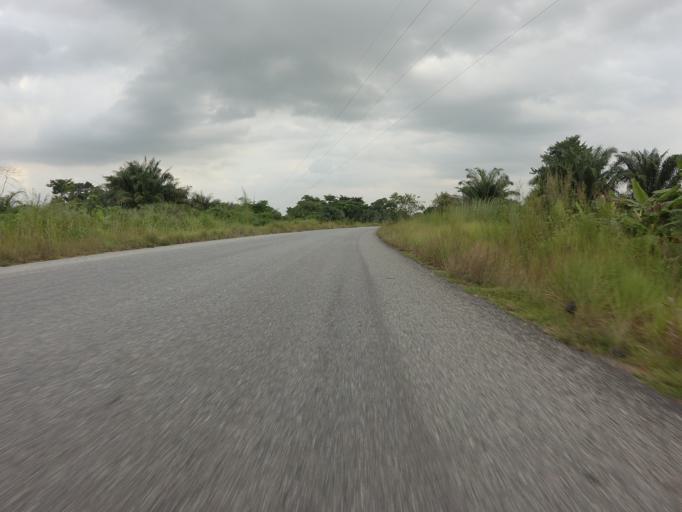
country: GH
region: Volta
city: Ho
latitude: 6.4783
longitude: 0.4959
